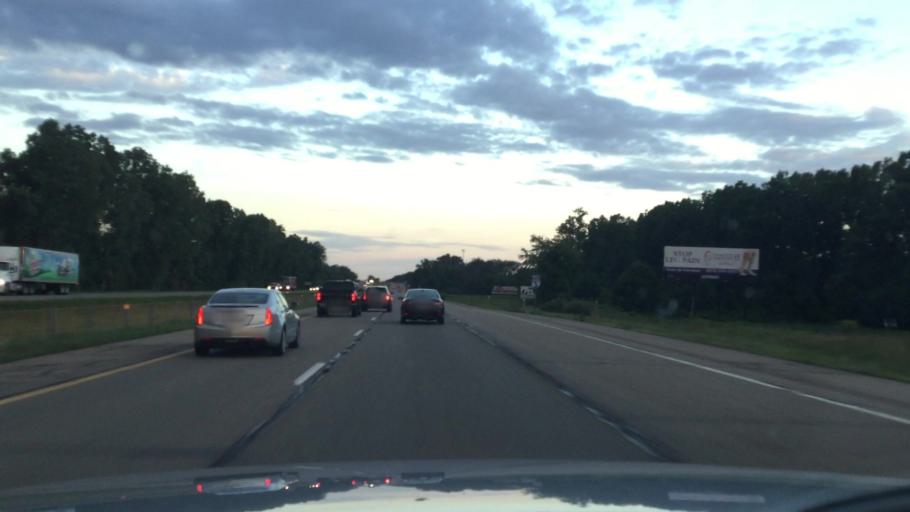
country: US
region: Michigan
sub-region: Shiawassee County
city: Durand
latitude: 42.9642
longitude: -83.9367
